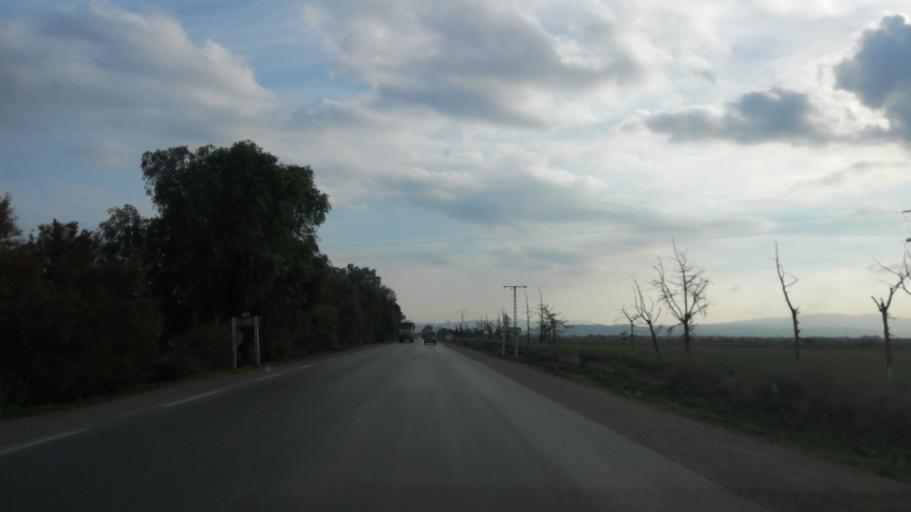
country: DZ
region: Mascara
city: Mascara
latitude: 35.6536
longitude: 0.0593
